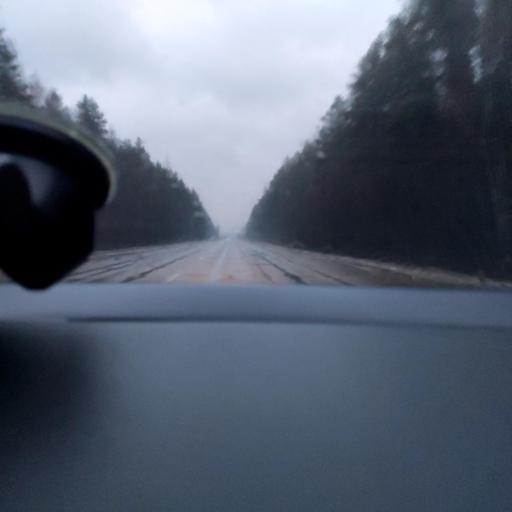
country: RU
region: Moskovskaya
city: Yegor'yevsk
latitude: 55.4270
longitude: 39.0342
